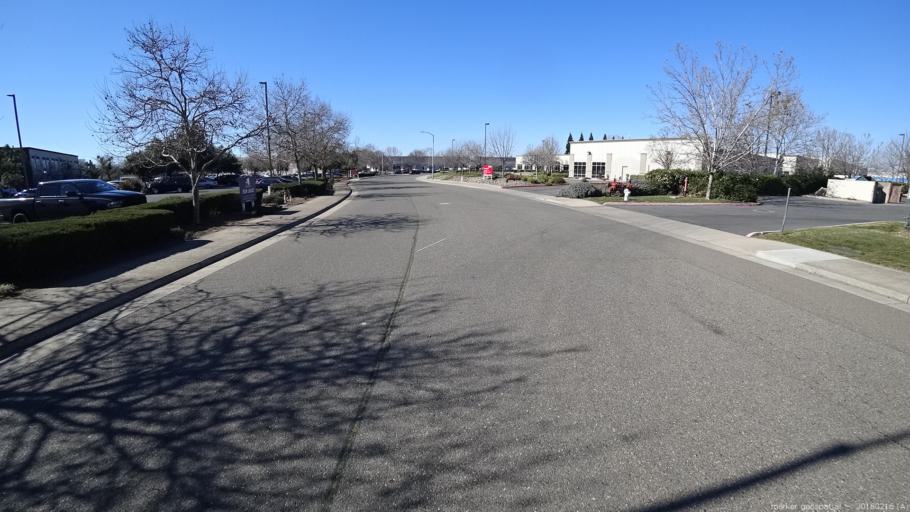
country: US
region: California
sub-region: Sacramento County
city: Gold River
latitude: 38.6138
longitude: -121.2615
